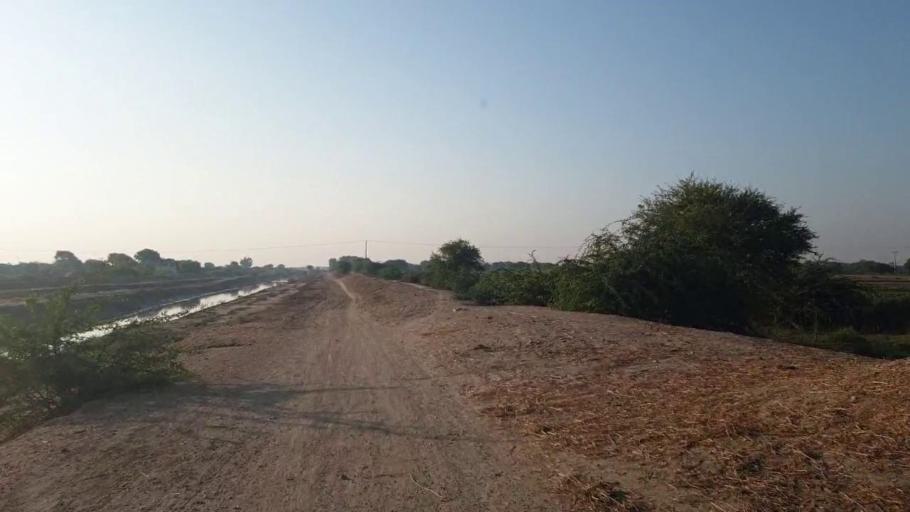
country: PK
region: Sindh
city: Badin
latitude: 24.6491
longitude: 68.7895
